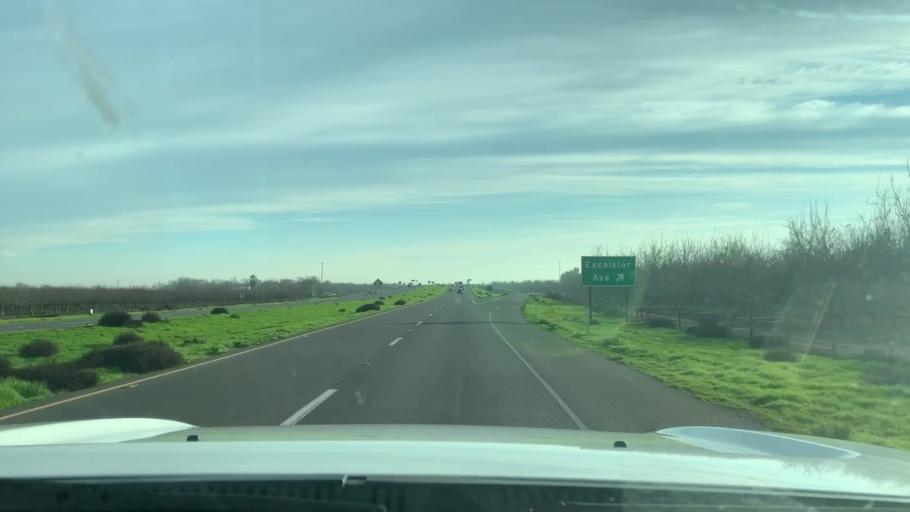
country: US
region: California
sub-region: Fresno County
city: Riverdale
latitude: 36.4065
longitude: -119.8062
